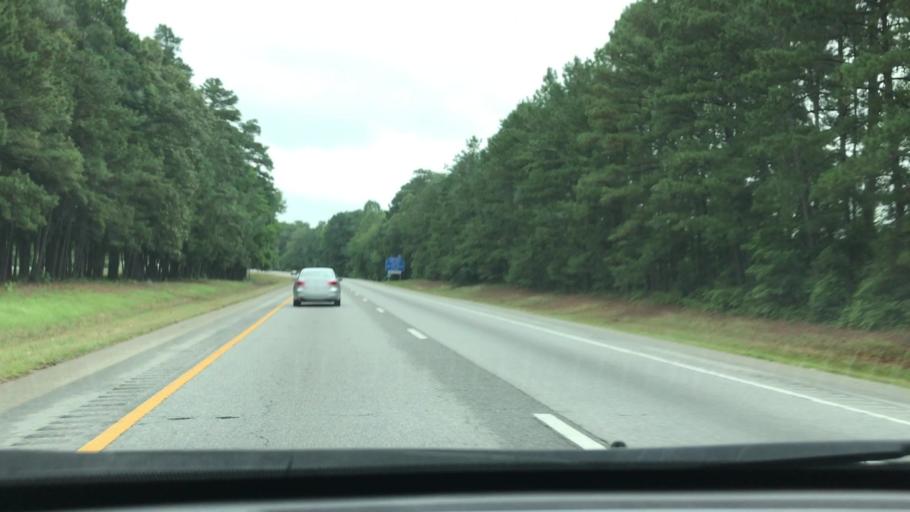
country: US
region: North Carolina
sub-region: Northampton County
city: Gaston
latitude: 36.5164
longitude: -77.5877
